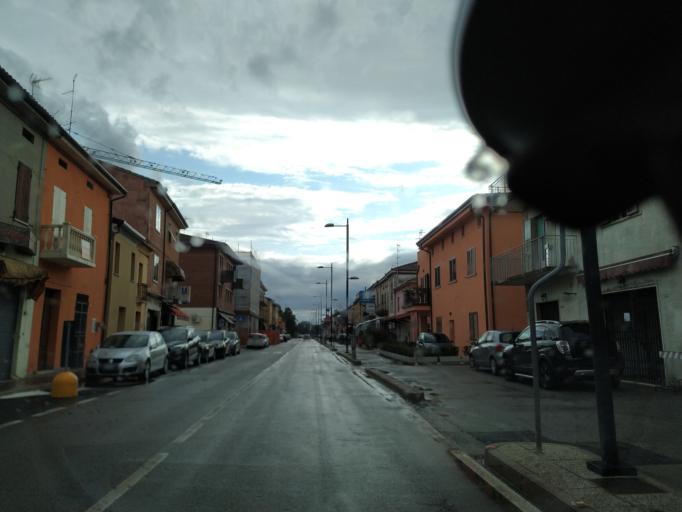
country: IT
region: Emilia-Romagna
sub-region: Provincia di Ferrara
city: Mirabello
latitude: 44.8256
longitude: 11.4602
